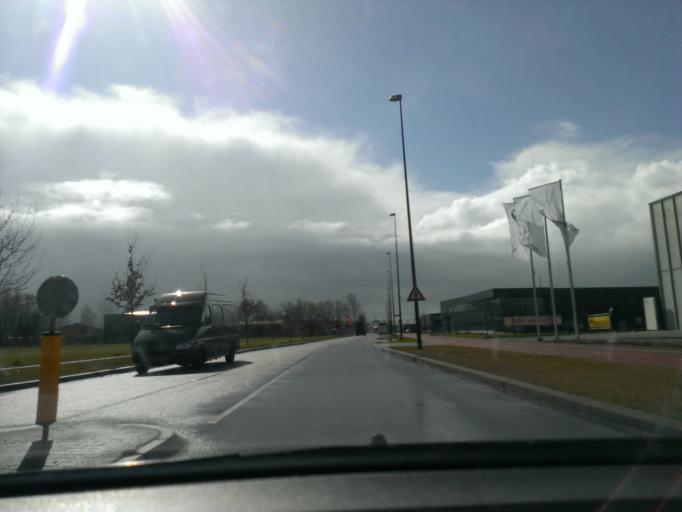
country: NL
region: Gelderland
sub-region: Gemeente Apeldoorn
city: Apeldoorn
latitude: 52.2470
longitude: 5.9712
